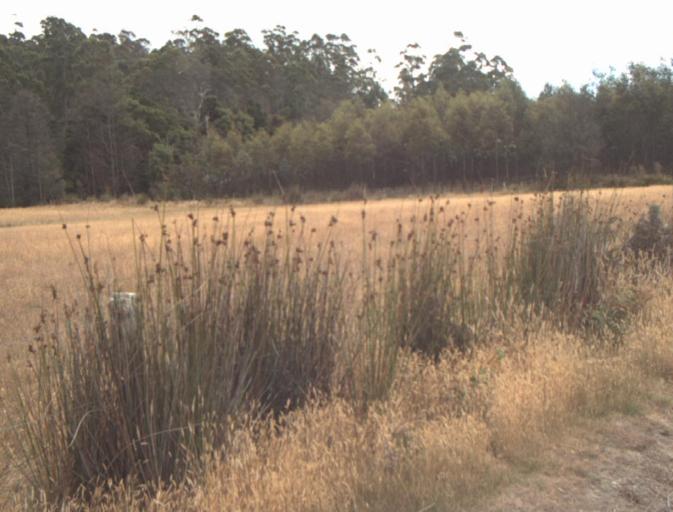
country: AU
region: Tasmania
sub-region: Launceston
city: Mayfield
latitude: -41.1896
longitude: 147.1676
